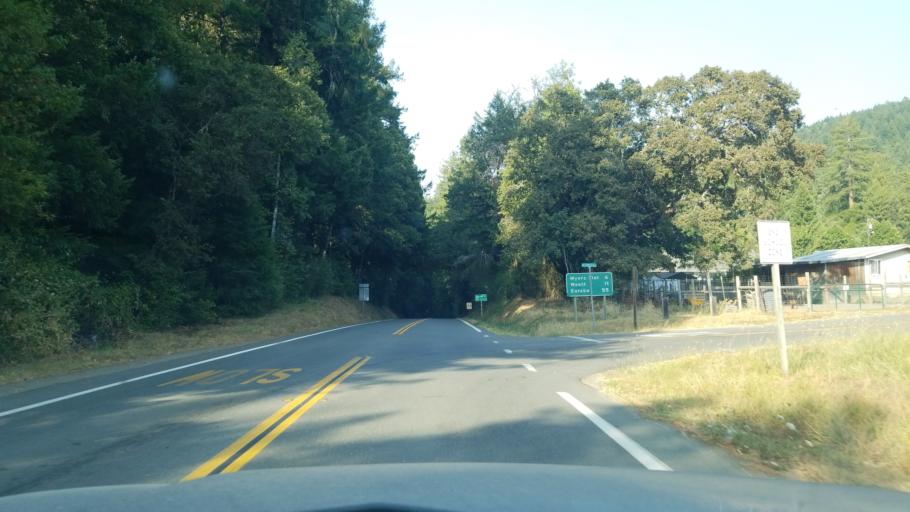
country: US
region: California
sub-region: Humboldt County
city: Redway
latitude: 40.2381
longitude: -123.8238
